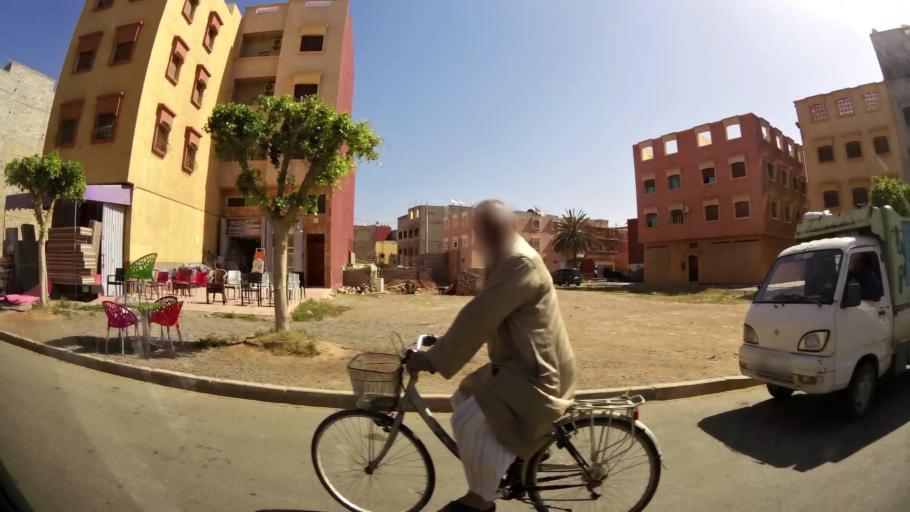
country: MA
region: Souss-Massa-Draa
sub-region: Inezgane-Ait Mellou
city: Inezgane
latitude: 30.3392
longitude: -9.5058
